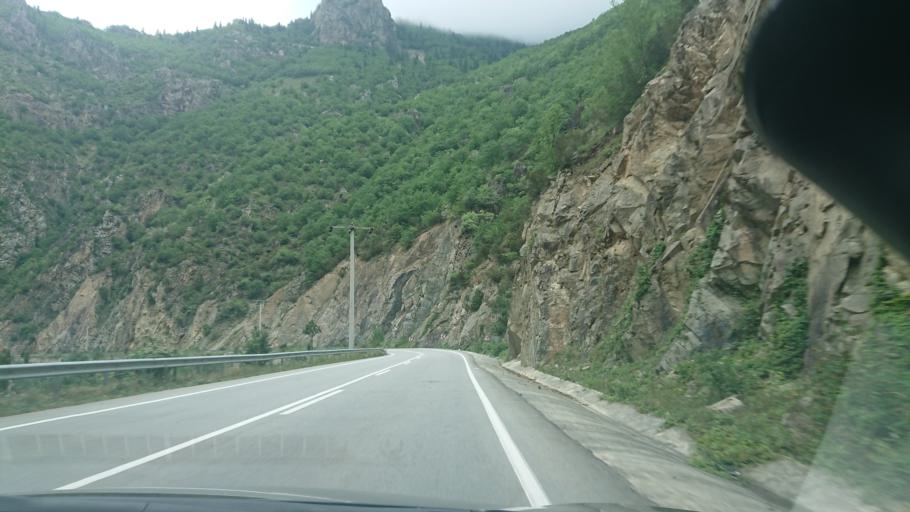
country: TR
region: Gumushane
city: Kurtun
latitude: 40.7238
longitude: 39.0224
